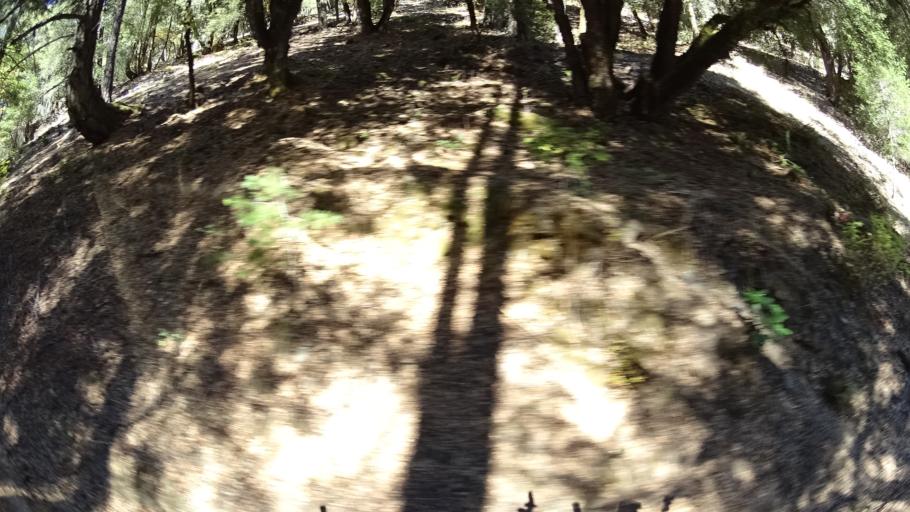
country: US
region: California
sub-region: Siskiyou County
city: Happy Camp
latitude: 41.3091
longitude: -123.1687
